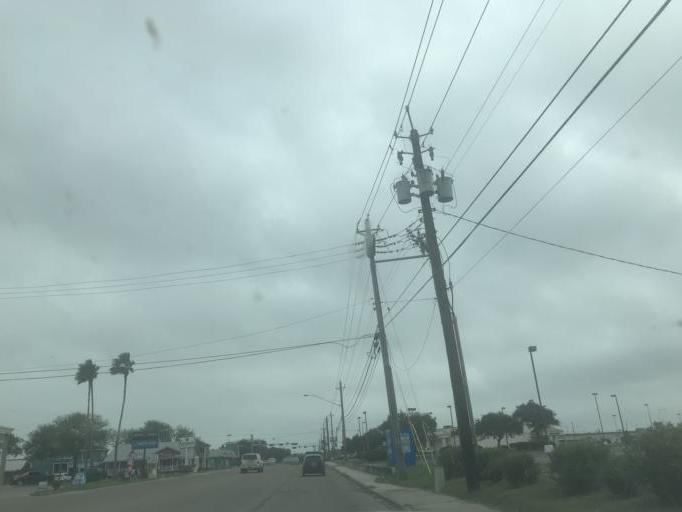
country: US
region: Texas
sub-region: Nueces County
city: Corpus Christi
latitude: 27.7092
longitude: -97.3647
